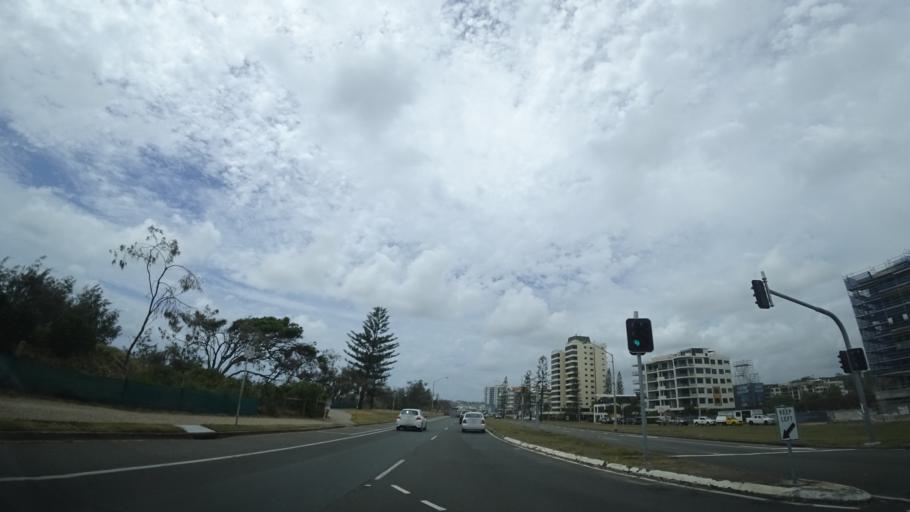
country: AU
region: Queensland
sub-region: Sunshine Coast
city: Mooloolaba
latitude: -26.6641
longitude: 153.1056
